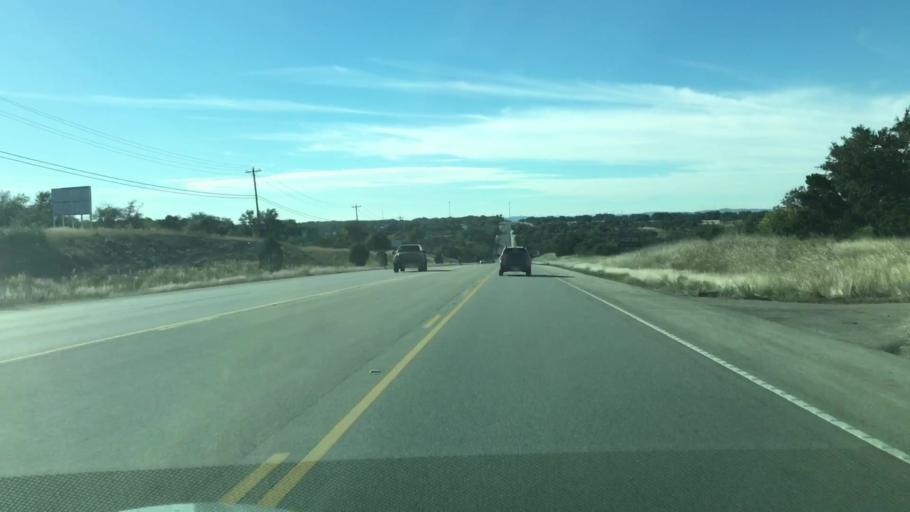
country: US
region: Texas
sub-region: Blanco County
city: Blanco
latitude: 29.9565
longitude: -98.4105
